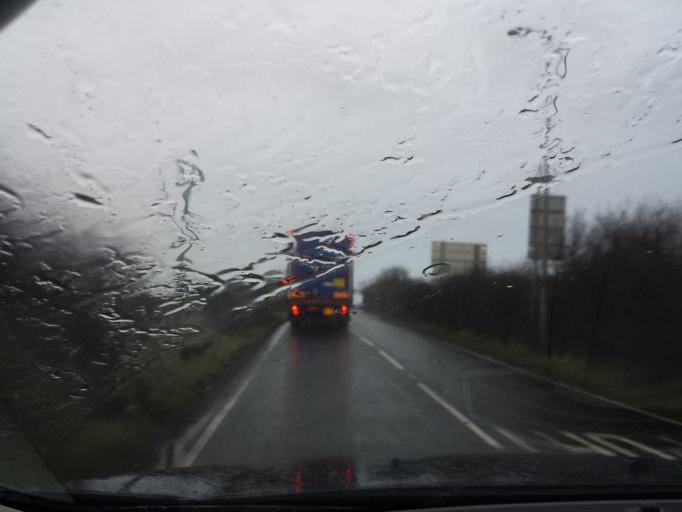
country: GB
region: Northern Ireland
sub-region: Antrim Borough
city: Antrim
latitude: 54.6643
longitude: -6.2202
